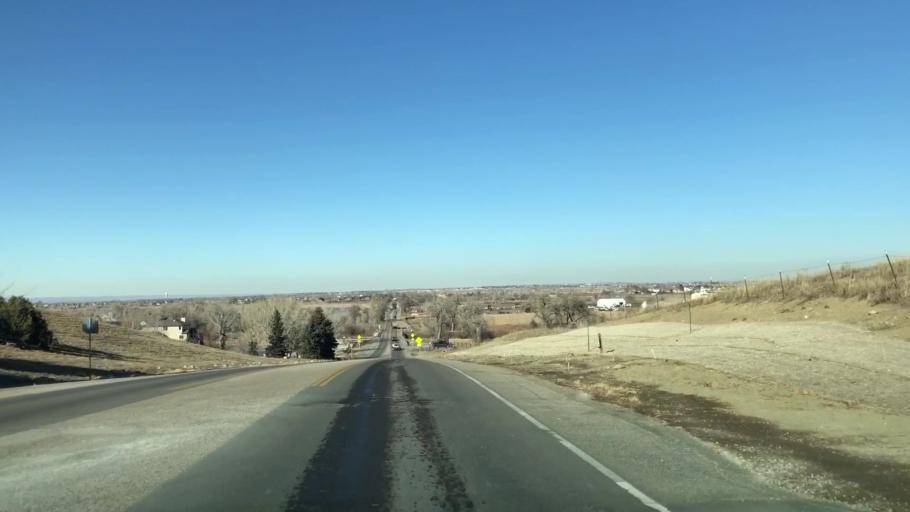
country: US
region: Colorado
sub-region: Weld County
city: Windsor
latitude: 40.4700
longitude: -104.9441
